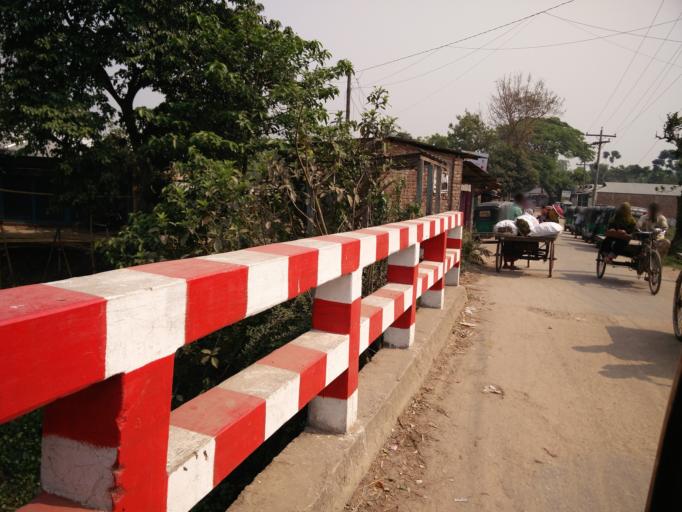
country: BD
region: Dhaka
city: Muktagacha
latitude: 24.9116
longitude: 90.2142
